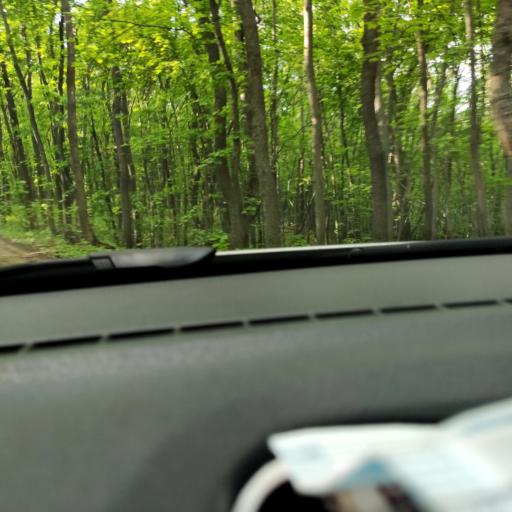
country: RU
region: Voronezj
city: Ramon'
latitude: 51.9429
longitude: 39.3702
